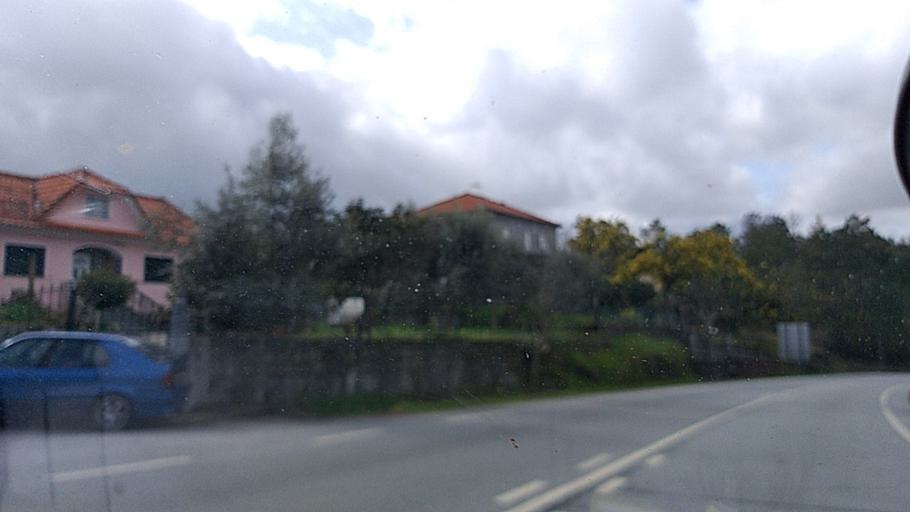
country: PT
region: Viseu
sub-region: Mangualde
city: Mangualde
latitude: 40.6551
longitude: -7.7299
